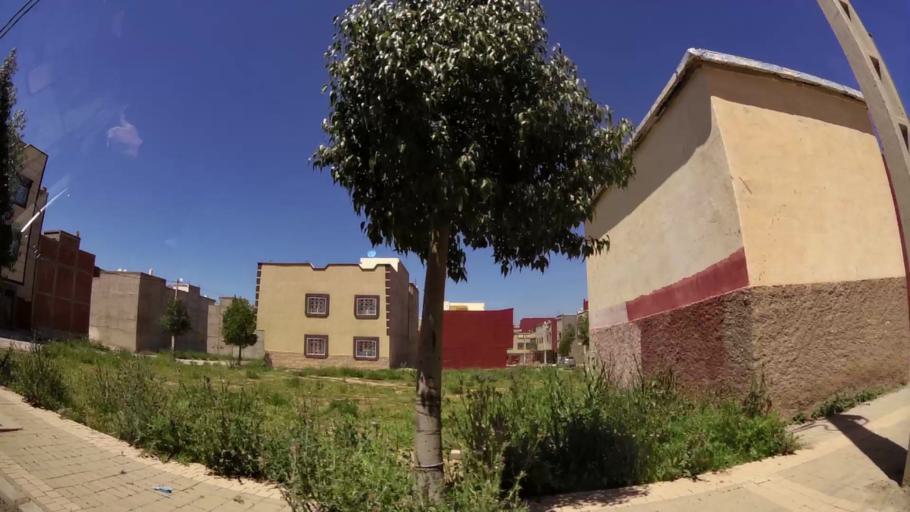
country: MA
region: Oriental
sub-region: Oujda-Angad
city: Oujda
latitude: 34.6844
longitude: -1.9470
